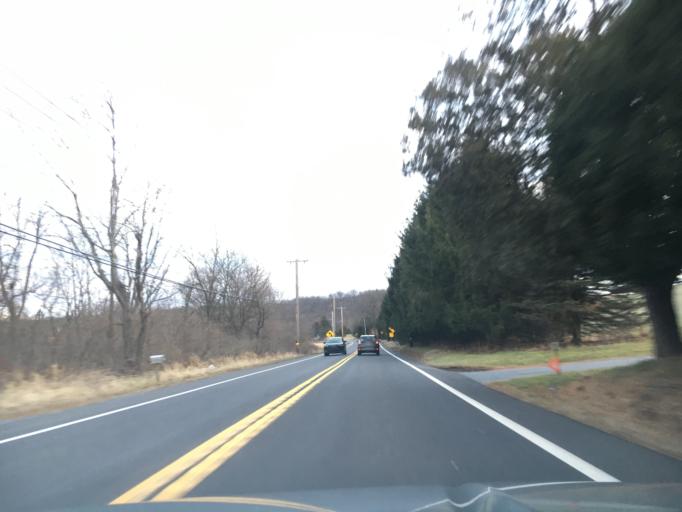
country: US
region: Pennsylvania
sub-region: Lehigh County
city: Schnecksville
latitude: 40.6777
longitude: -75.6453
